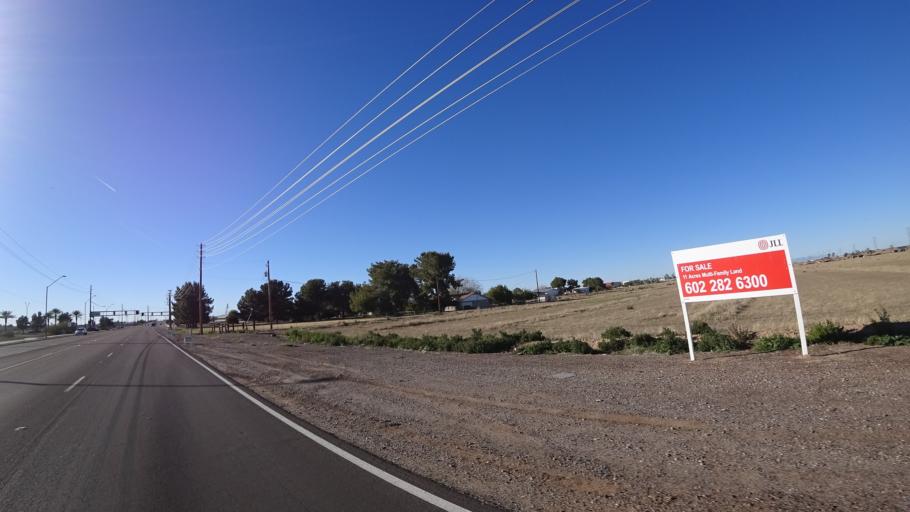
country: US
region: Arizona
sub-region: Maricopa County
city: Avondale
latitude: 33.4496
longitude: -112.3216
